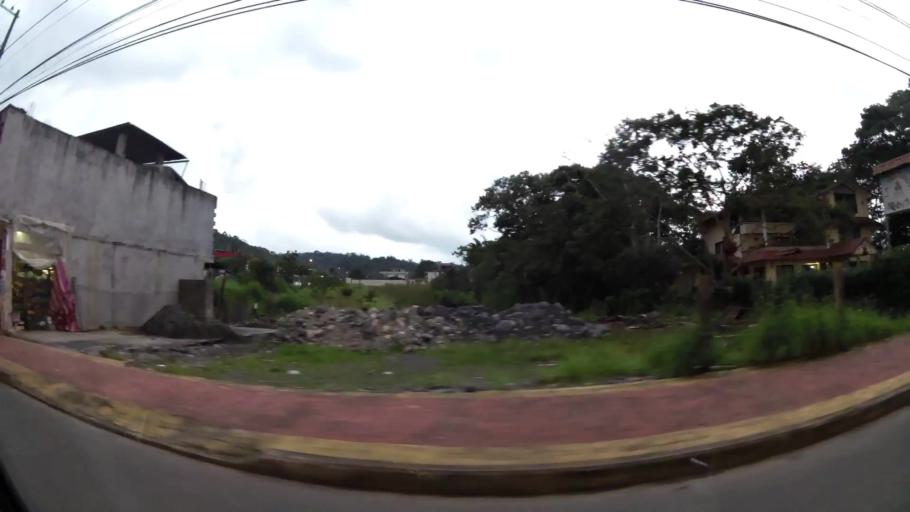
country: EC
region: Pastaza
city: Puyo
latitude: -1.4888
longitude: -78.0104
